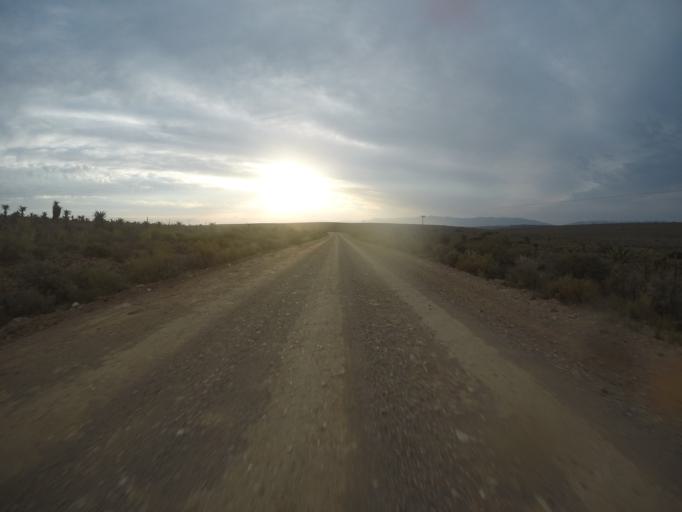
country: ZA
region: Eastern Cape
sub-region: Cacadu District Municipality
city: Willowmore
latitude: -33.5770
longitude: 23.1739
